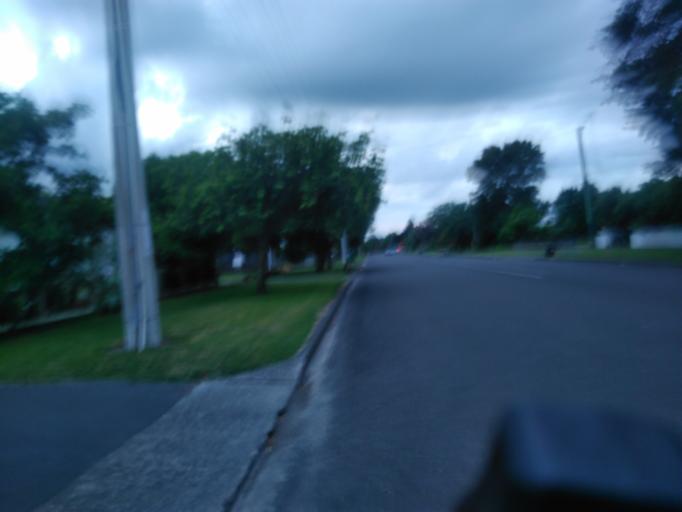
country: NZ
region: Gisborne
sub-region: Gisborne District
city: Gisborne
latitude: -38.6531
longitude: 178.0214
